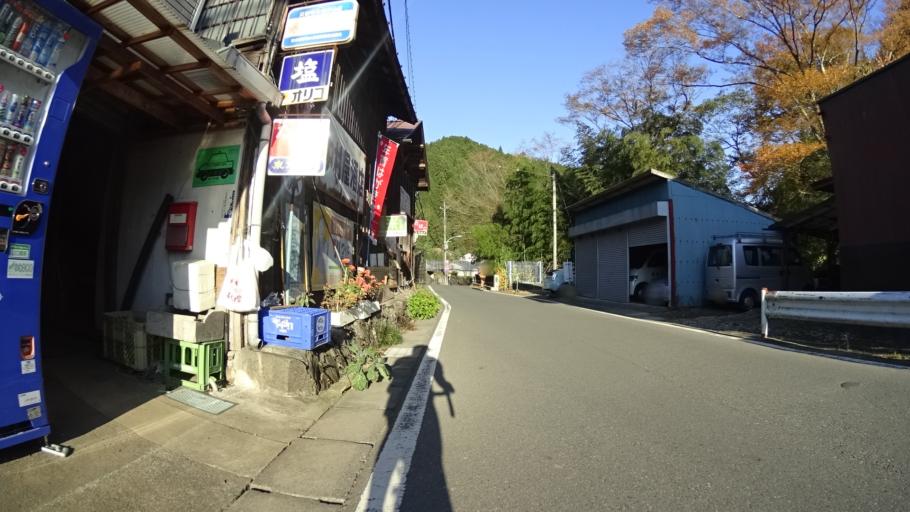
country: JP
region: Tokyo
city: Itsukaichi
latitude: 35.6740
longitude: 139.2204
